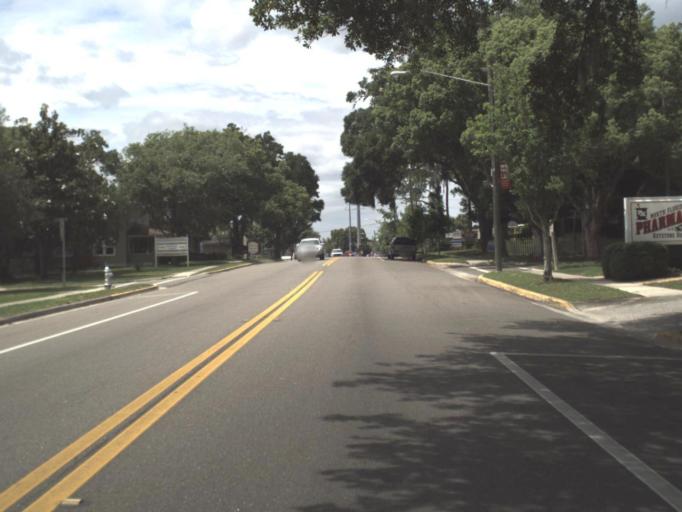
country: US
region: Florida
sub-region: Clay County
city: Keystone Heights
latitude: 29.7821
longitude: -82.0307
